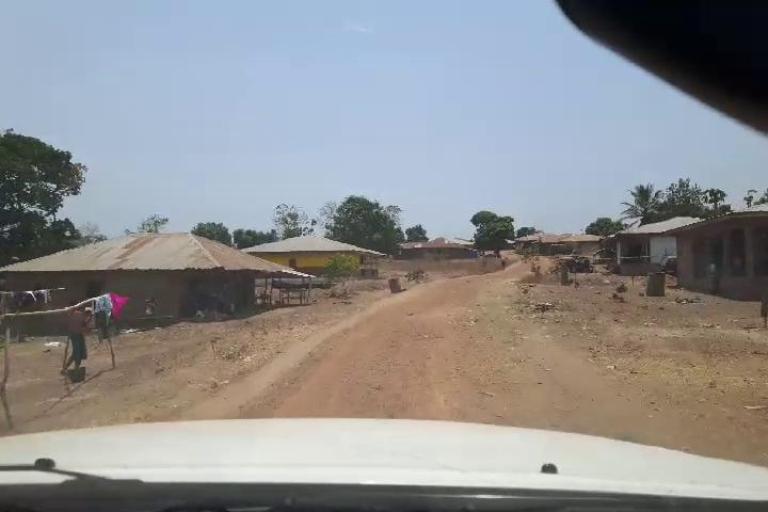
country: SL
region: Northern Province
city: Alikalia
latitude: 9.0628
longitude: -11.4873
